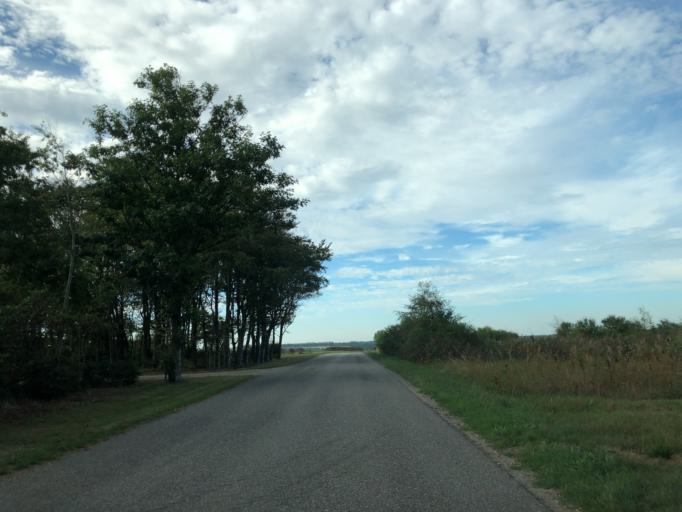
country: DK
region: Central Jutland
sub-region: Holstebro Kommune
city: Ulfborg
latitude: 56.1506
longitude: 8.4068
